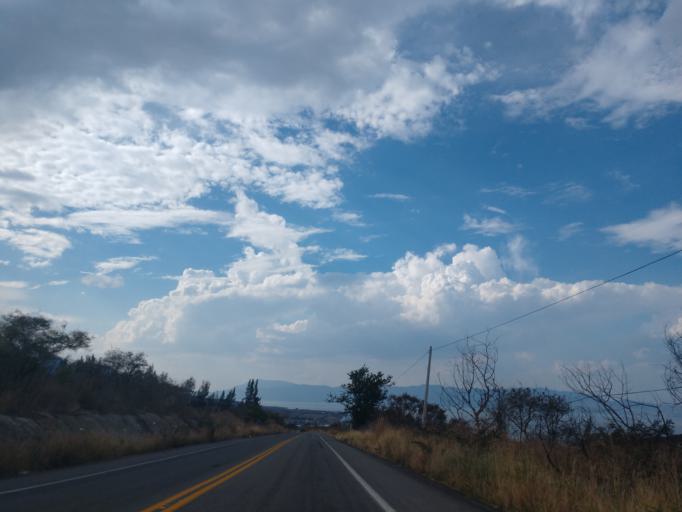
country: MX
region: Jalisco
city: La Manzanilla de la Paz
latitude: 20.1305
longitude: -103.1662
